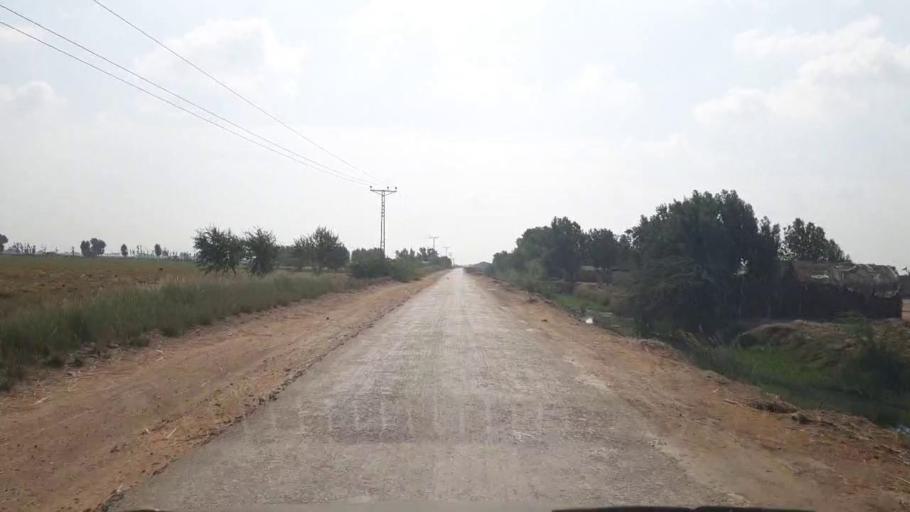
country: PK
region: Sindh
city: Kario
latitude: 24.6458
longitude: 68.5425
